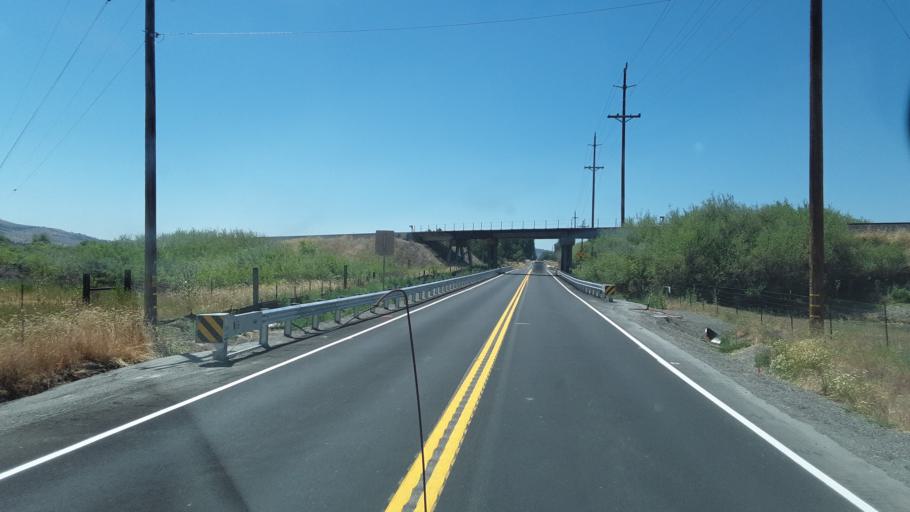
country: US
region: Oregon
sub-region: Klamath County
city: Altamont
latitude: 42.1471
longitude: -121.6983
